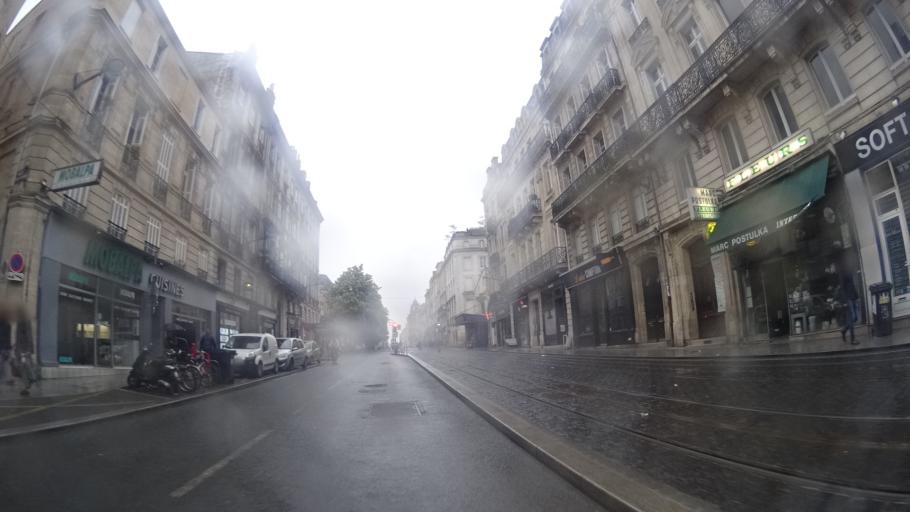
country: FR
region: Aquitaine
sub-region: Departement de la Gironde
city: Bordeaux
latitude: 44.8370
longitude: -0.5760
